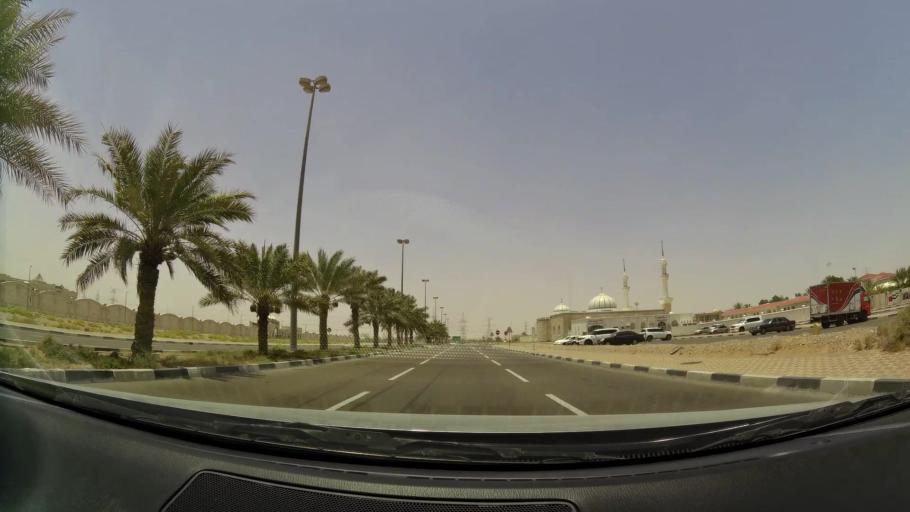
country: OM
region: Al Buraimi
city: Al Buraymi
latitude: 24.2697
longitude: 55.7206
